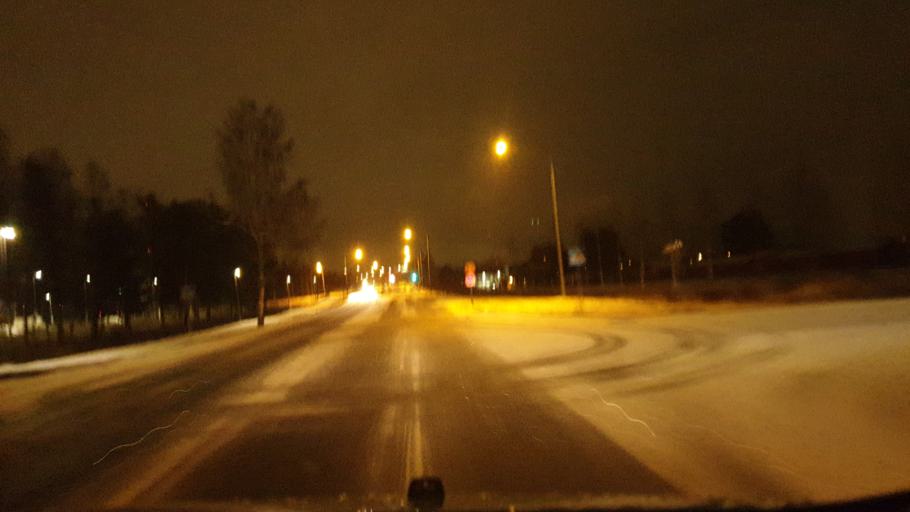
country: FI
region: Northern Ostrobothnia
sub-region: Oulu
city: Oulu
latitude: 64.9837
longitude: 25.4656
